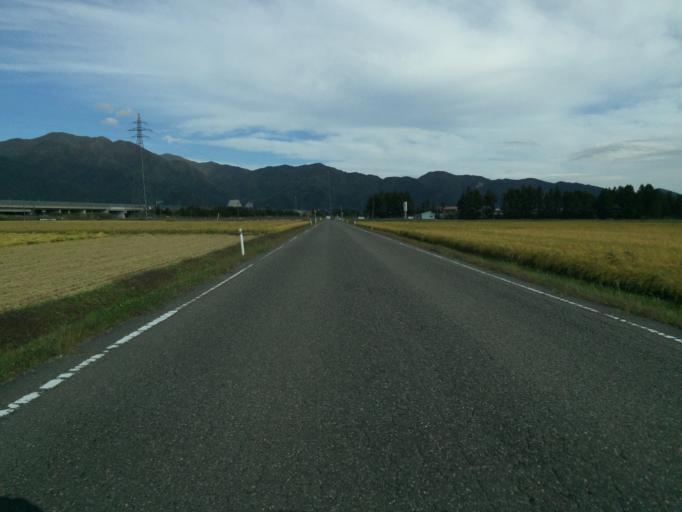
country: JP
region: Fukushima
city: Inawashiro
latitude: 37.5427
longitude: 140.1008
